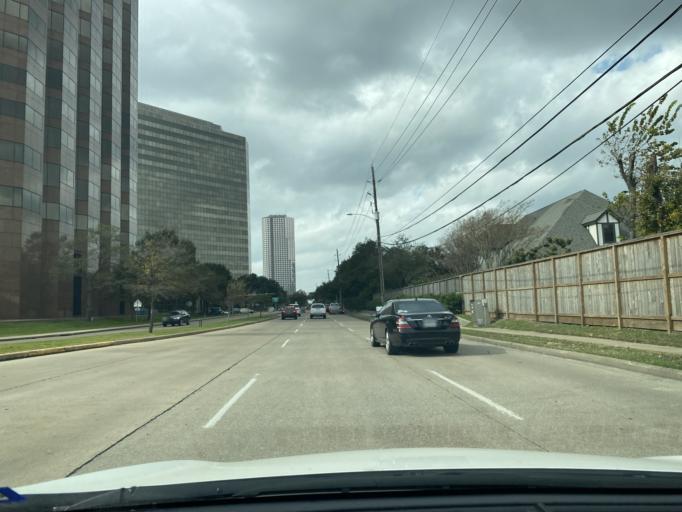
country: US
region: Texas
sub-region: Harris County
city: Hunters Creek Village
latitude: 29.7502
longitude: -95.4710
